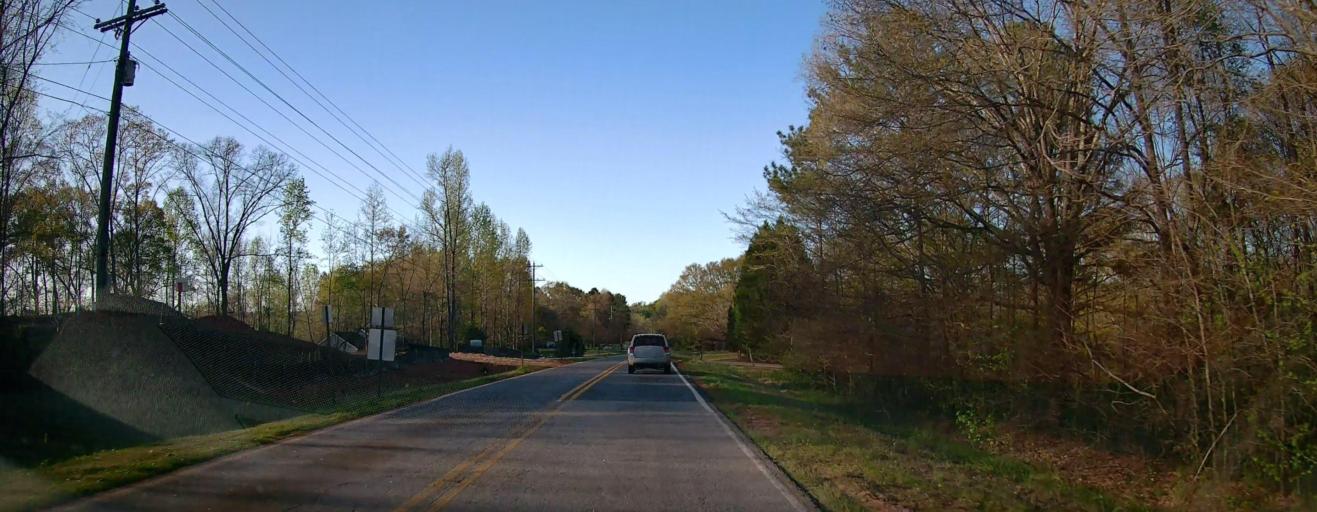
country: US
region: Georgia
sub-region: Newton County
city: Porterdale
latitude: 33.5722
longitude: -83.9044
